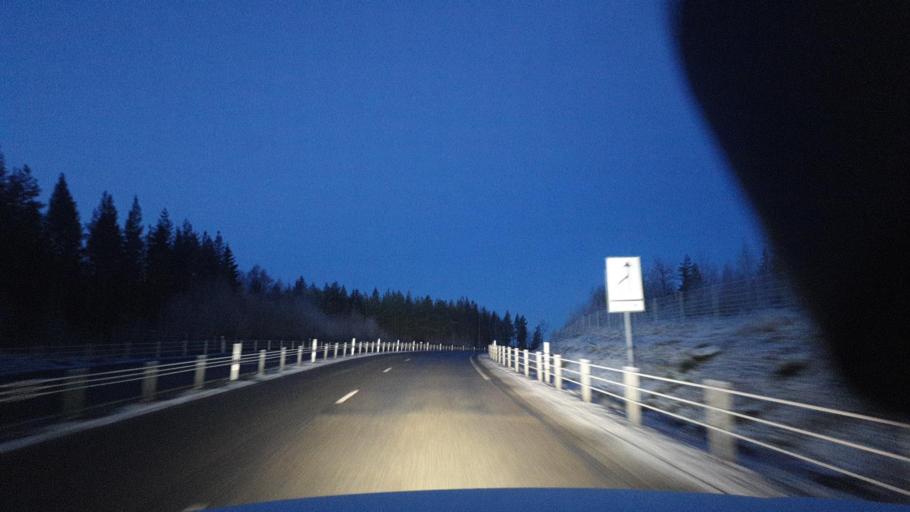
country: SE
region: Vaermland
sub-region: Eda Kommun
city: Amotfors
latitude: 59.7593
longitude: 12.4659
